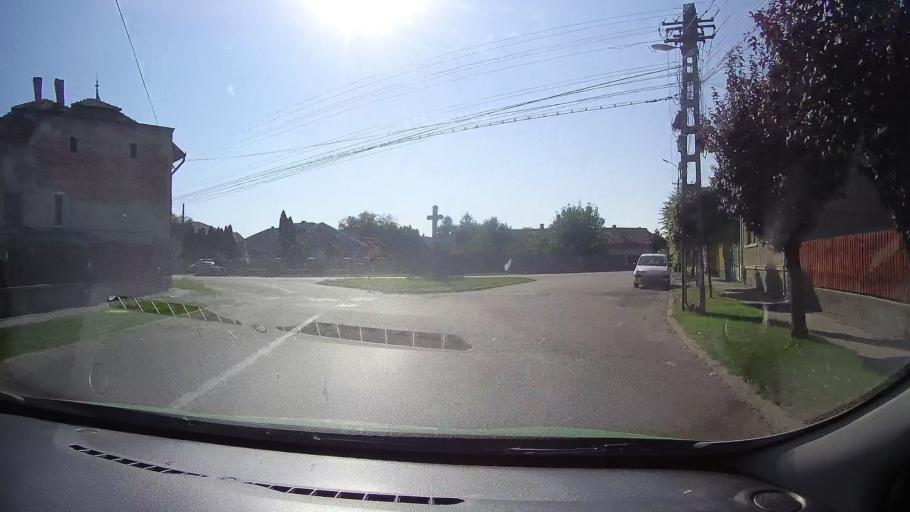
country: RO
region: Satu Mare
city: Carei
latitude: 47.6892
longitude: 22.4712
